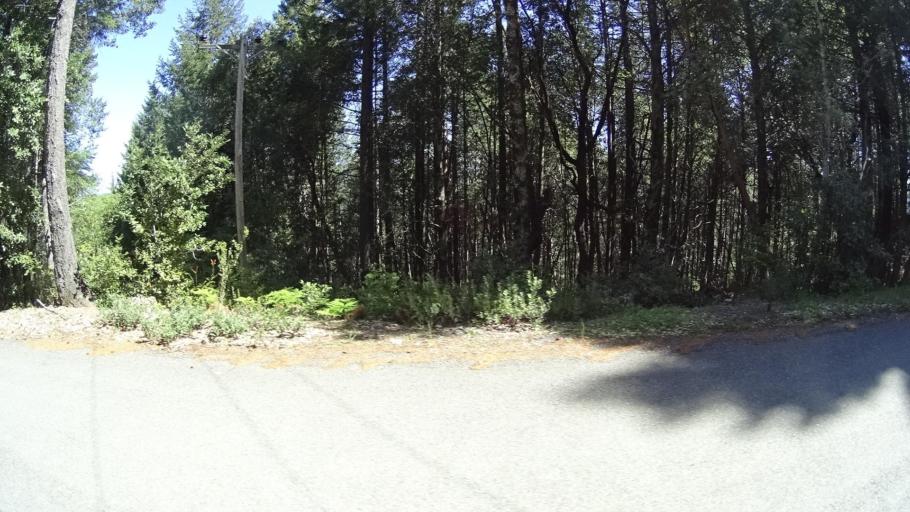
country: US
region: California
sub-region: Humboldt County
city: Redway
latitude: 40.1885
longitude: -124.0936
